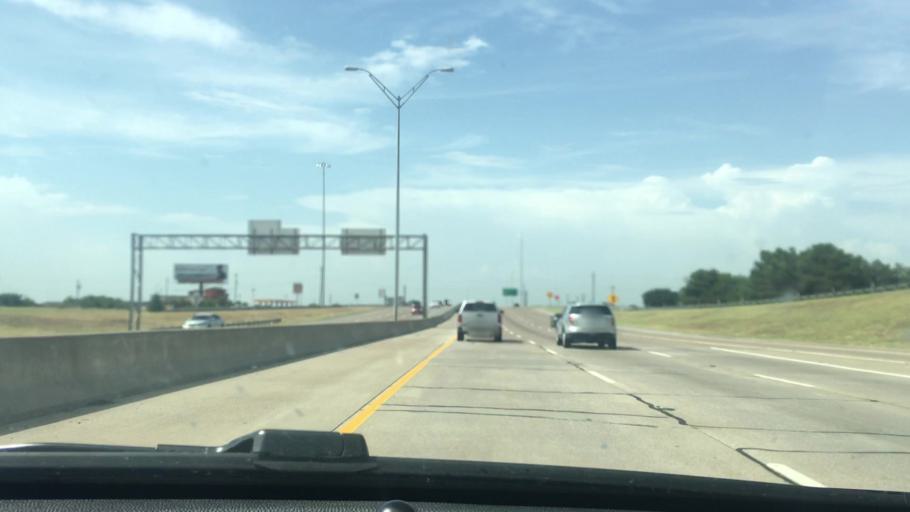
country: US
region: Texas
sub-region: Dallas County
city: DeSoto
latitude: 32.6449
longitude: -96.8232
